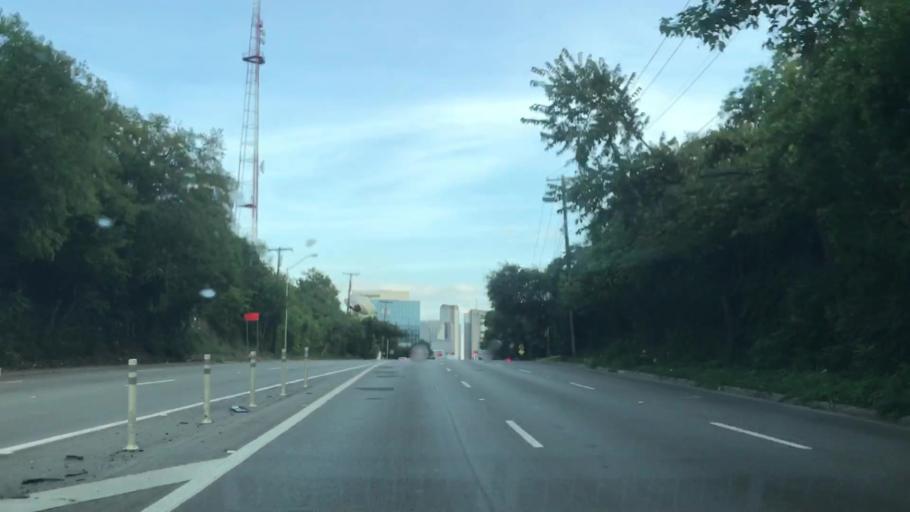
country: US
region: Texas
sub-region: Dallas County
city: Dallas
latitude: 32.7967
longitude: -96.8124
